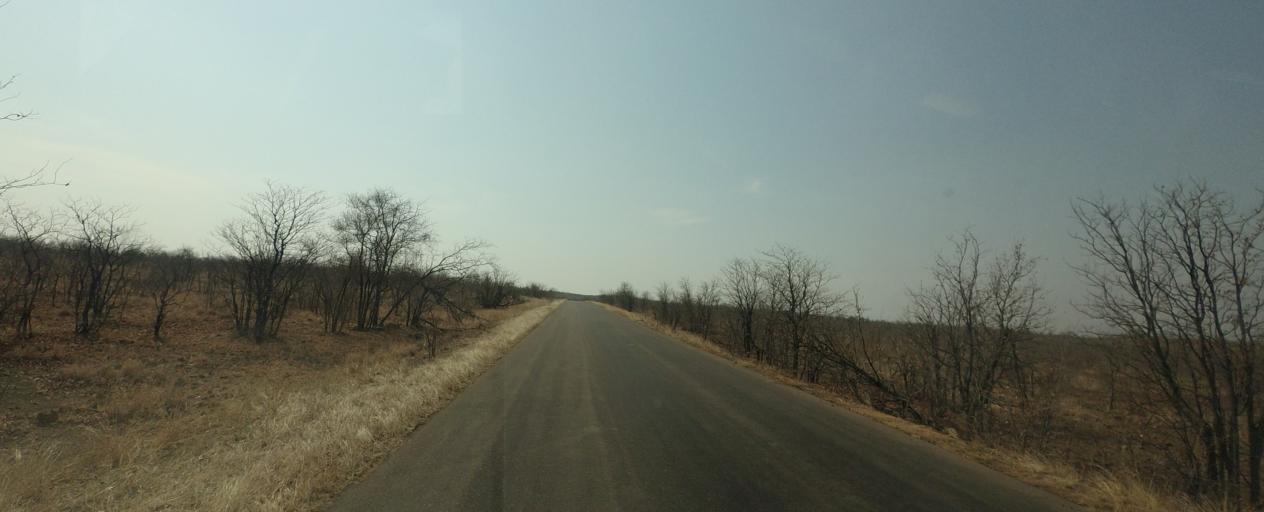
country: ZA
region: Limpopo
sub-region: Mopani District Municipality
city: Phalaborwa
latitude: -23.9753
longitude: 31.6363
